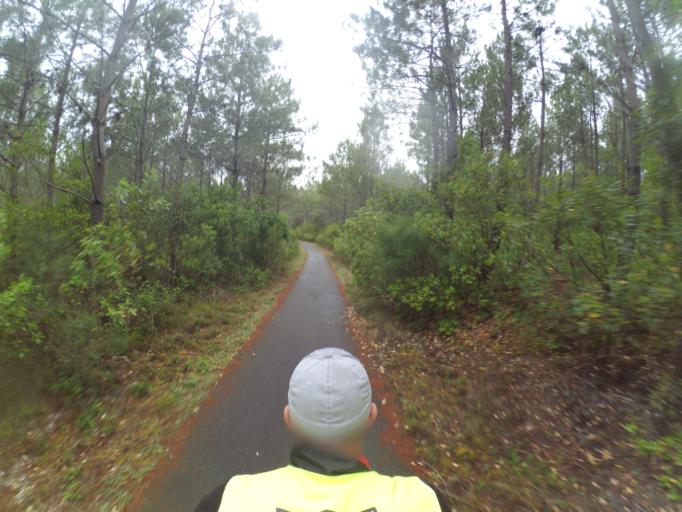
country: FR
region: Aquitaine
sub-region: Departement des Landes
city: Mimizan
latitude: 44.2216
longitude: -1.2555
